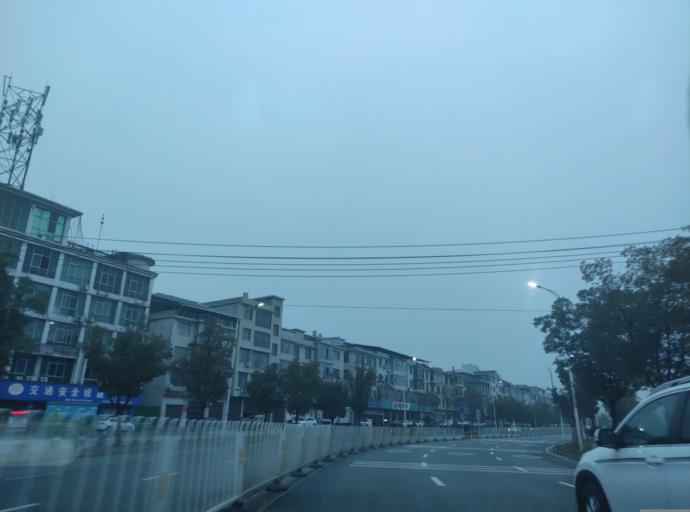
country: CN
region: Jiangxi Sheng
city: Pingxiang
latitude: 27.6687
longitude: 113.8704
